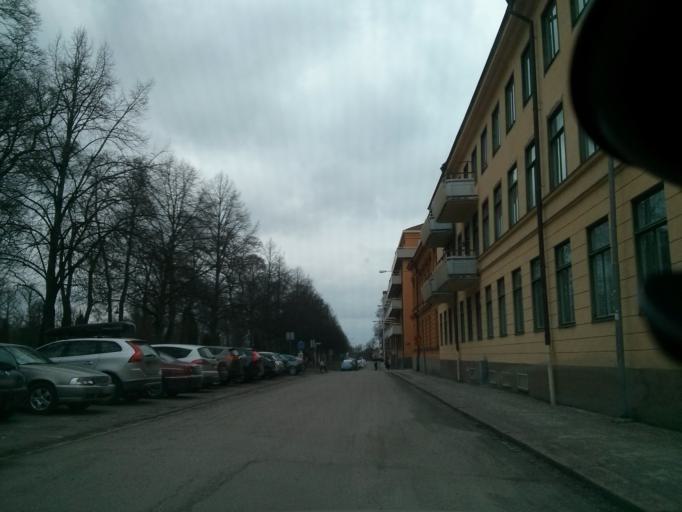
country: SE
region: Uppsala
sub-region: Uppsala Kommun
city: Uppsala
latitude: 59.8554
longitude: 17.6296
